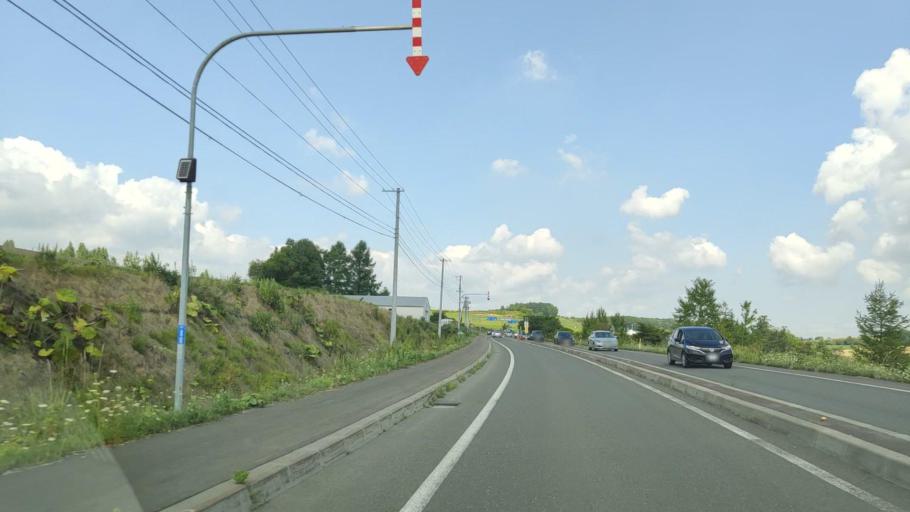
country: JP
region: Hokkaido
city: Shimo-furano
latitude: 43.5308
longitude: 142.4436
